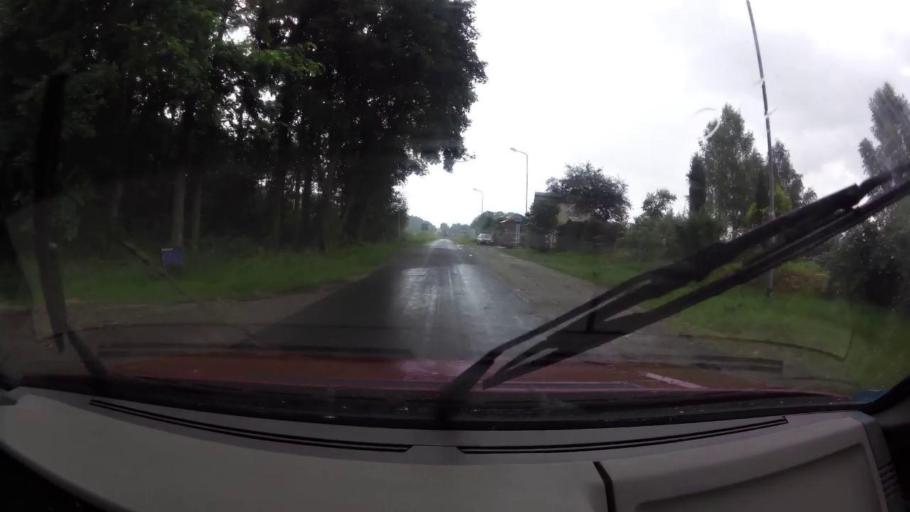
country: PL
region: West Pomeranian Voivodeship
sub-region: Koszalin
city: Koszalin
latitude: 54.0763
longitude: 16.1242
